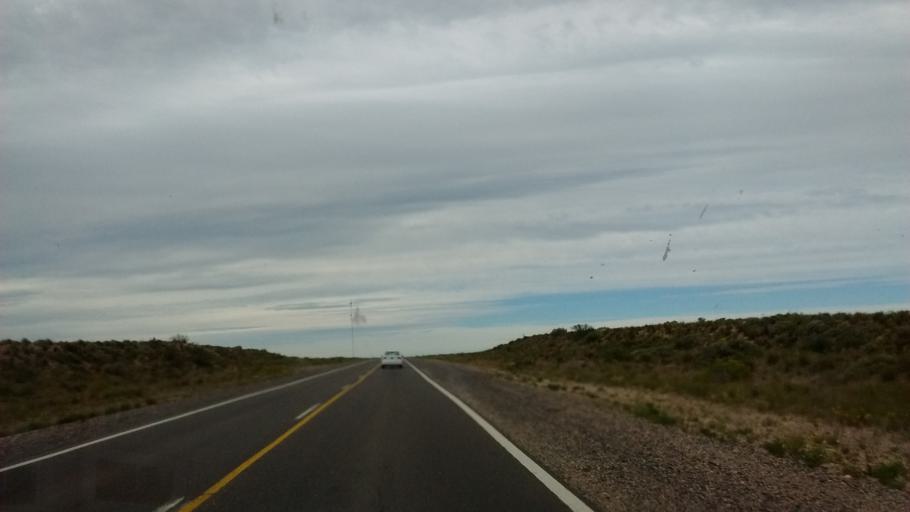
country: AR
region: Rio Negro
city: Contraalmirante Cordero
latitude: -38.3129
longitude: -68.0039
